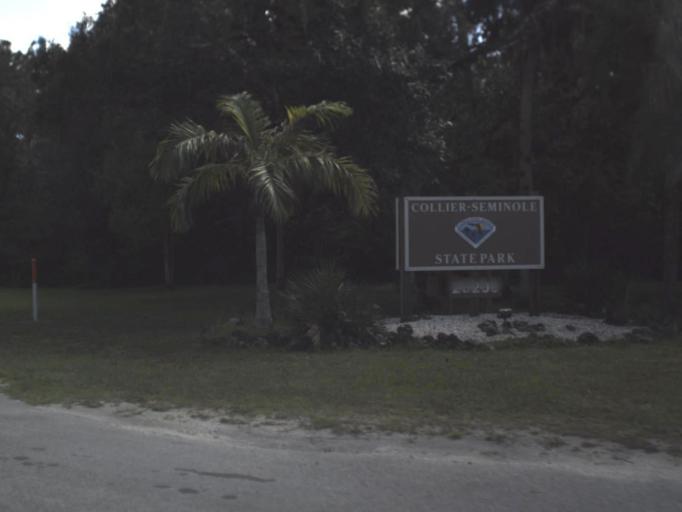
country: US
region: Florida
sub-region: Collier County
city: Lely Resort
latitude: 25.9923
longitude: -81.5899
